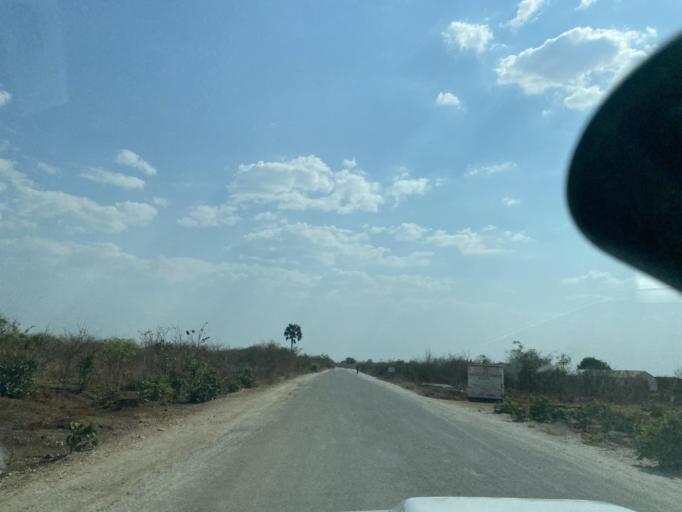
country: ZM
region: Lusaka
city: Lusaka
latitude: -15.3690
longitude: 28.0822
